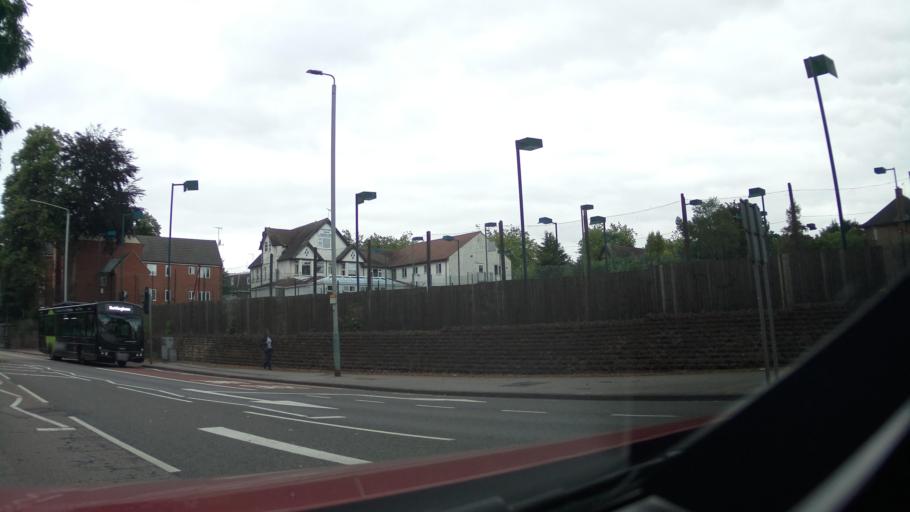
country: GB
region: England
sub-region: Nottinghamshire
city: Arnold
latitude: 52.9891
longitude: -1.1404
